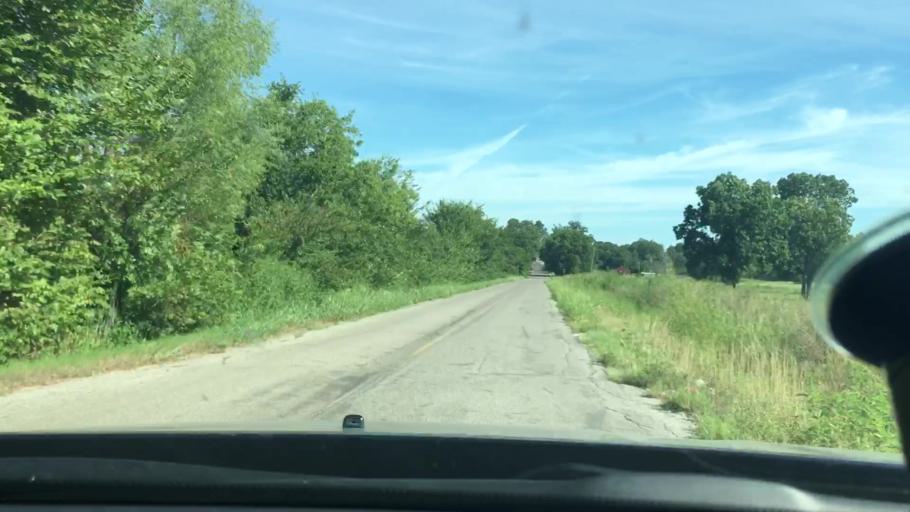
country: US
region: Oklahoma
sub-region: Carter County
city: Lone Grove
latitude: 34.2871
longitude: -97.2826
